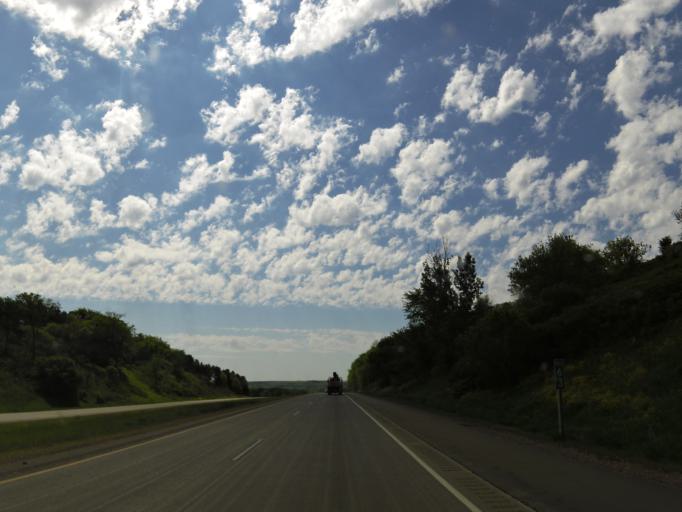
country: US
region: Wisconsin
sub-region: Eau Claire County
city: Eau Claire
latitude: 44.8023
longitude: -91.5559
